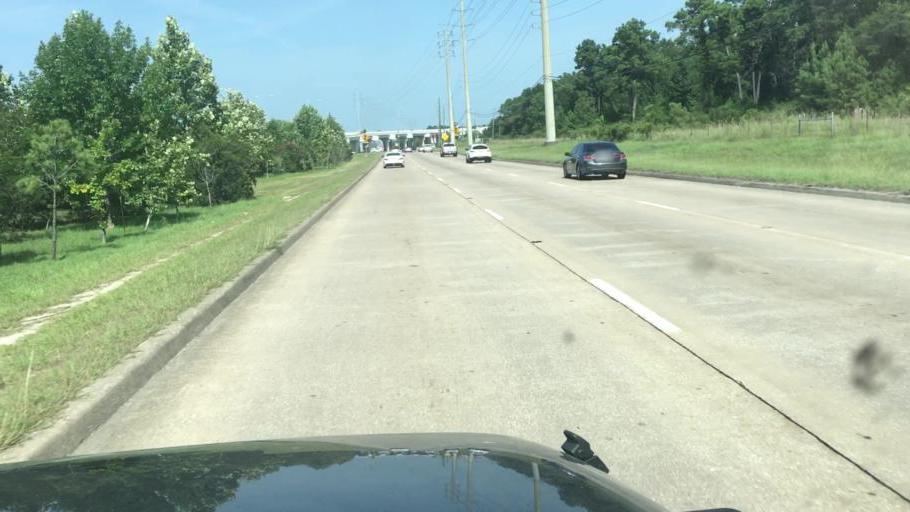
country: US
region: Texas
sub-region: Harris County
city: Atascocita
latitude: 29.9339
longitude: -95.2155
